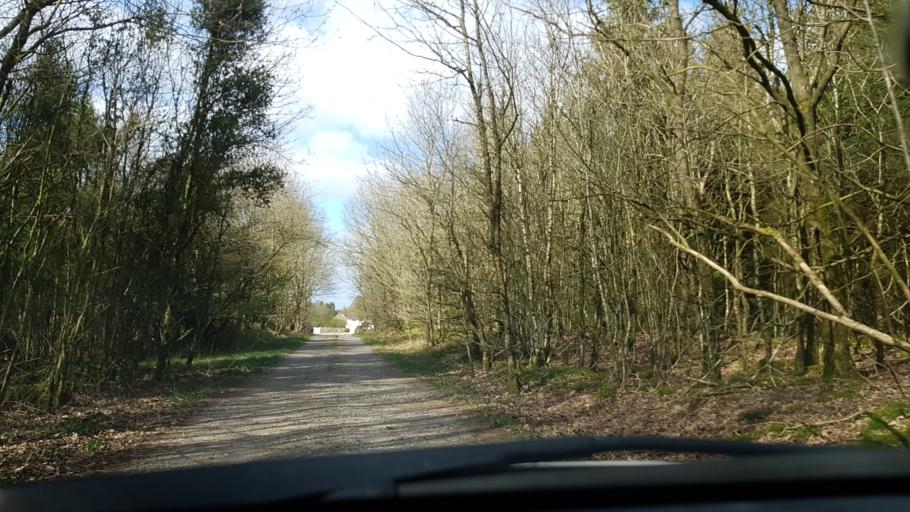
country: DK
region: South Denmark
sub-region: Haderslev Kommune
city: Gram
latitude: 55.2972
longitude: 8.9847
